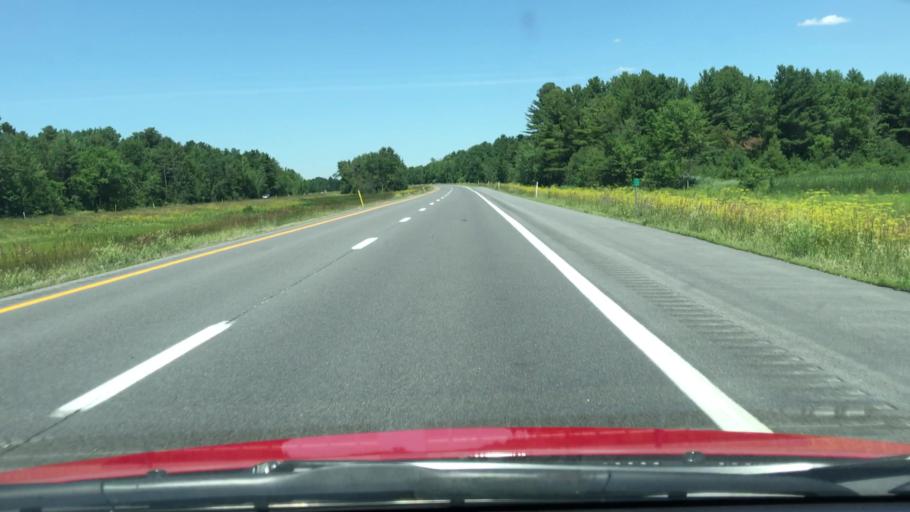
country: US
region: New York
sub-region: Clinton County
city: Cumberland Head
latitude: 44.8391
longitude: -73.4463
